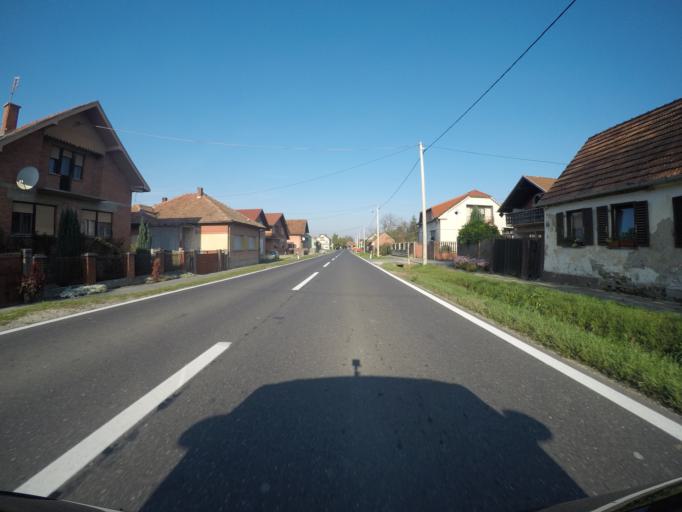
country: HR
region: Koprivnicko-Krizevacka
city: Virje
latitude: 46.0267
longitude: 16.9925
